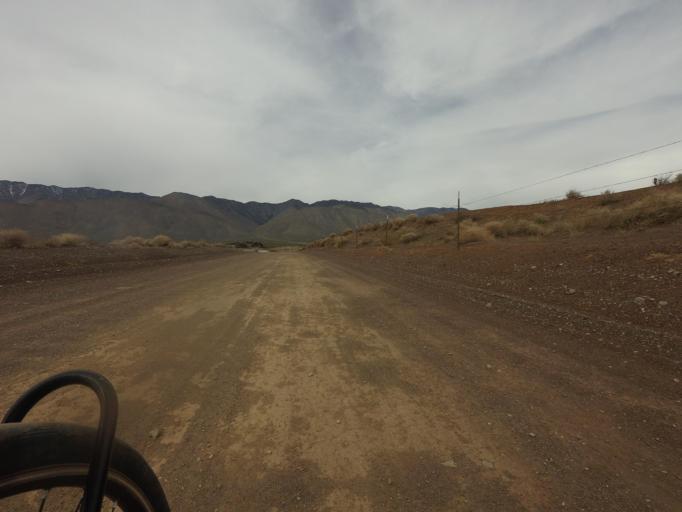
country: US
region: California
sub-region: Kern County
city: Inyokern
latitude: 35.9773
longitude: -117.9164
